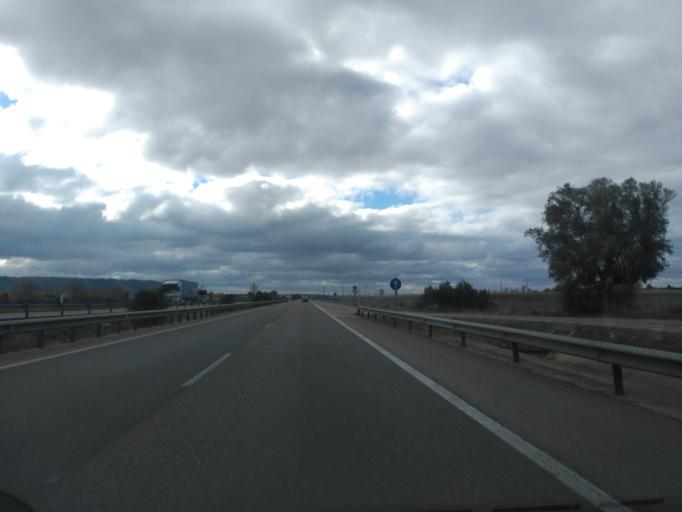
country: ES
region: Castille and Leon
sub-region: Provincia de Valladolid
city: Cabezon
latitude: 41.7752
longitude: -4.6188
